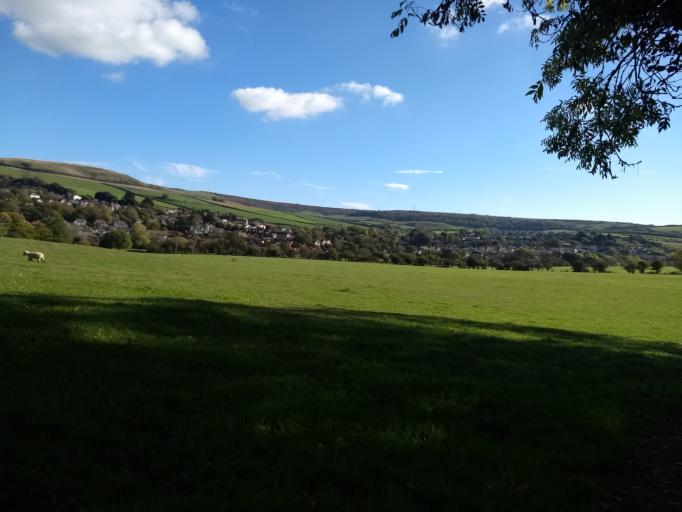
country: GB
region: England
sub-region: Isle of Wight
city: Ventnor
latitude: 50.6178
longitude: -1.2327
